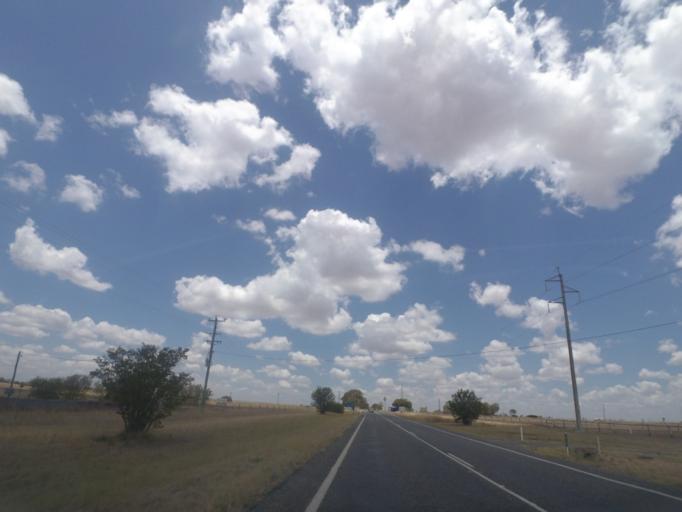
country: AU
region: Queensland
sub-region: Southern Downs
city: Warwick
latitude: -27.9298
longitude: 151.9857
